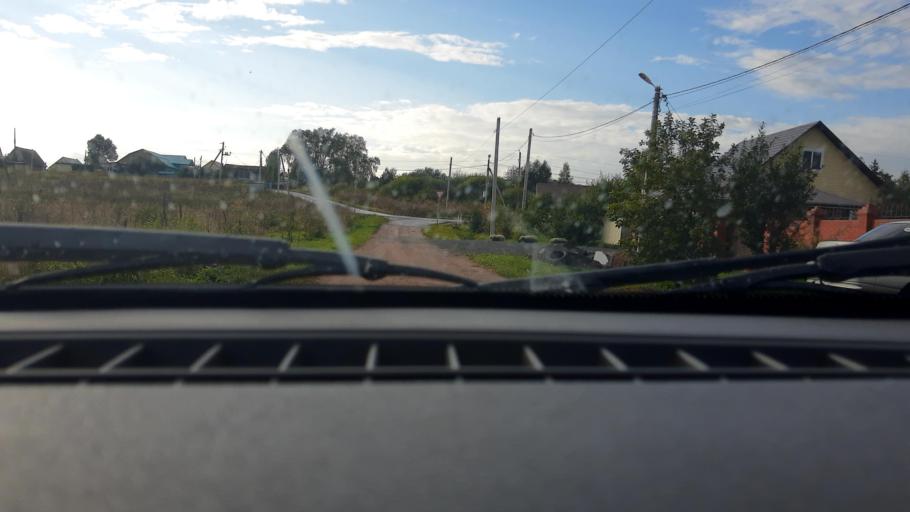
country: RU
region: Bashkortostan
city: Mikhaylovka
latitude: 54.7845
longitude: 55.8111
